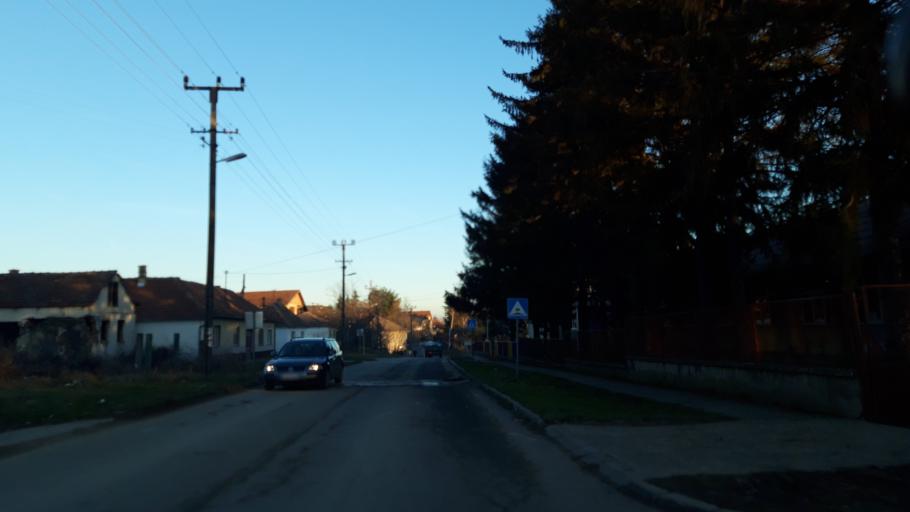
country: RS
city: Cortanovci
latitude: 45.1566
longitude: 20.0162
